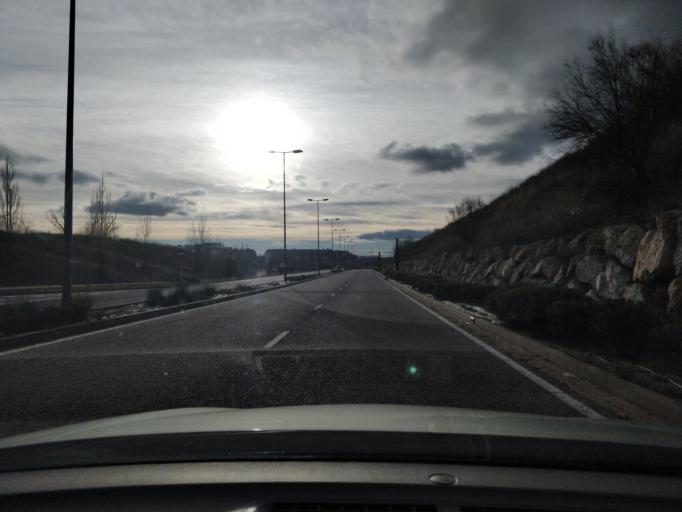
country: ES
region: Castille and Leon
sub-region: Provincia de Burgos
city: Burgos
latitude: 42.3486
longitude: -3.7202
